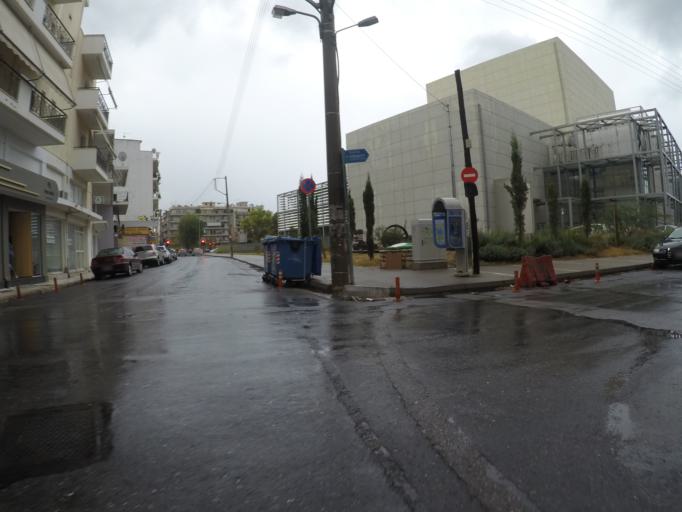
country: GR
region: Peloponnese
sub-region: Nomos Messinias
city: Kalamata
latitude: 37.0404
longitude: 22.1073
